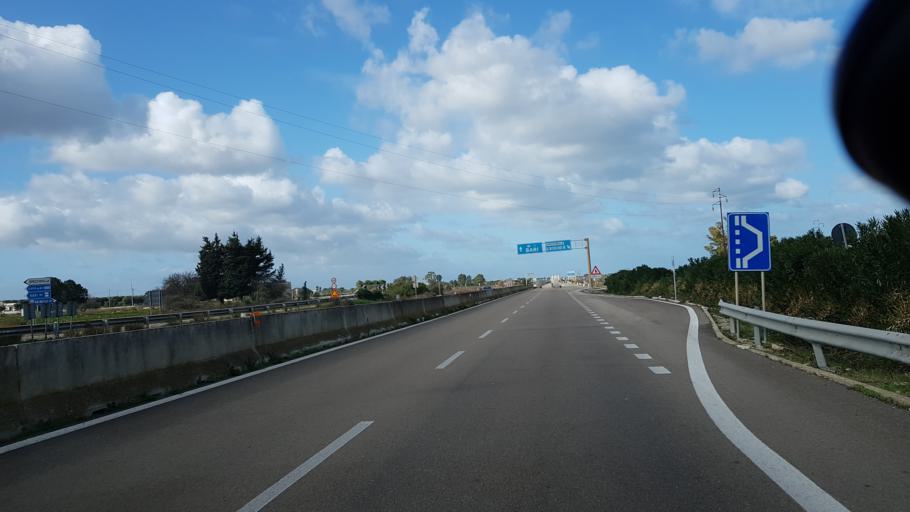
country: IT
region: Apulia
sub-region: Provincia di Brindisi
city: San Vito dei Normanni
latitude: 40.7277
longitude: 17.7391
